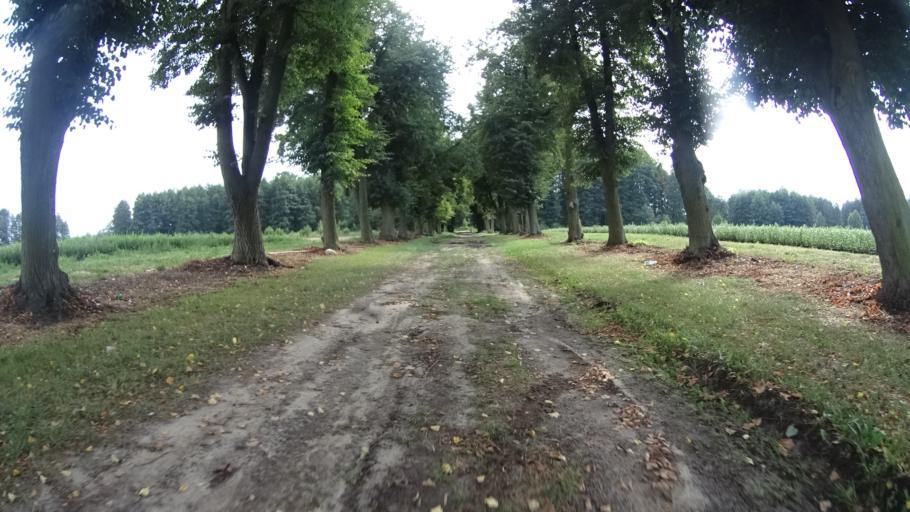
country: PL
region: Masovian Voivodeship
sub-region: Powiat grojecki
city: Goszczyn
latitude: 51.6945
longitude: 20.8238
